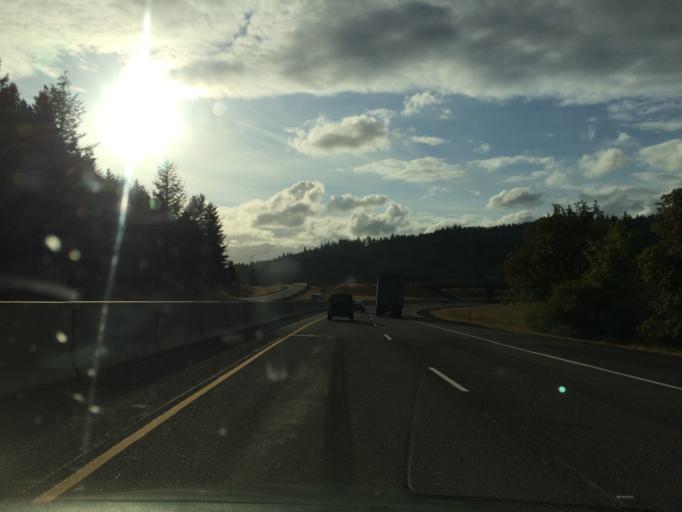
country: US
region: Oregon
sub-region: Douglas County
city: Drain
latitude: 43.7071
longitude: -123.2140
